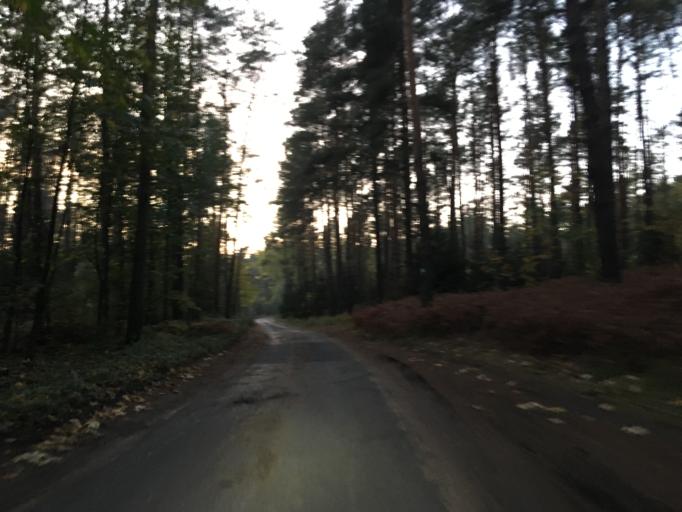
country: DE
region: Brandenburg
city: Glienicke
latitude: 52.6813
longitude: 13.3366
